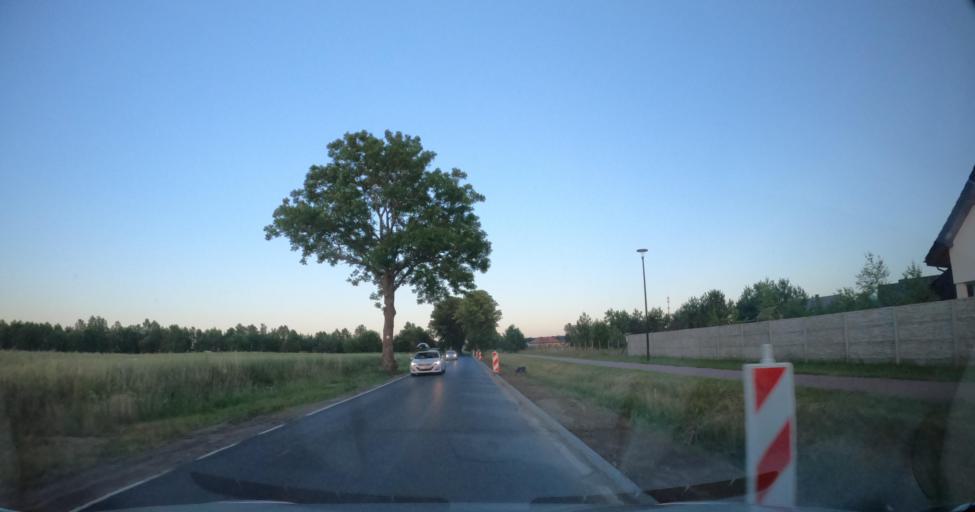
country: PL
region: Pomeranian Voivodeship
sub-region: Powiat wejherowski
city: Linia
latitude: 54.4536
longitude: 17.9206
